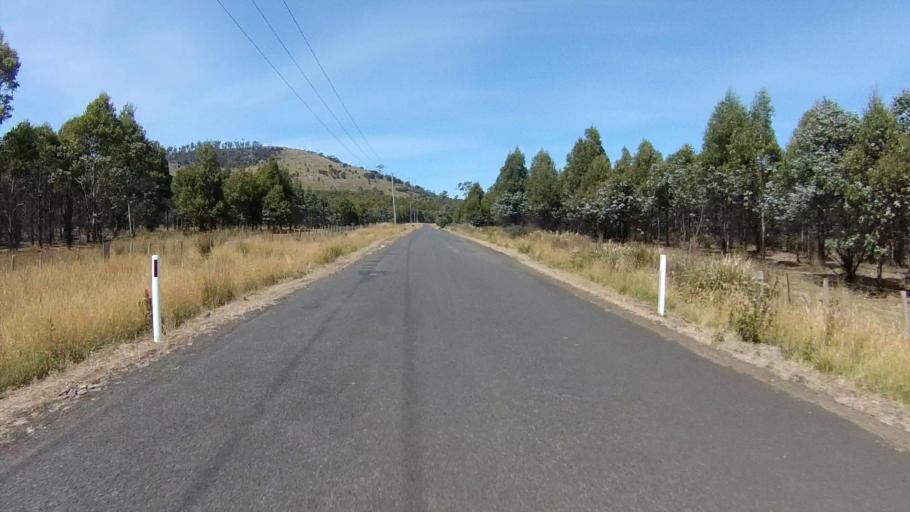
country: AU
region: Tasmania
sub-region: Sorell
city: Sorell
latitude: -42.6210
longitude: 147.7297
